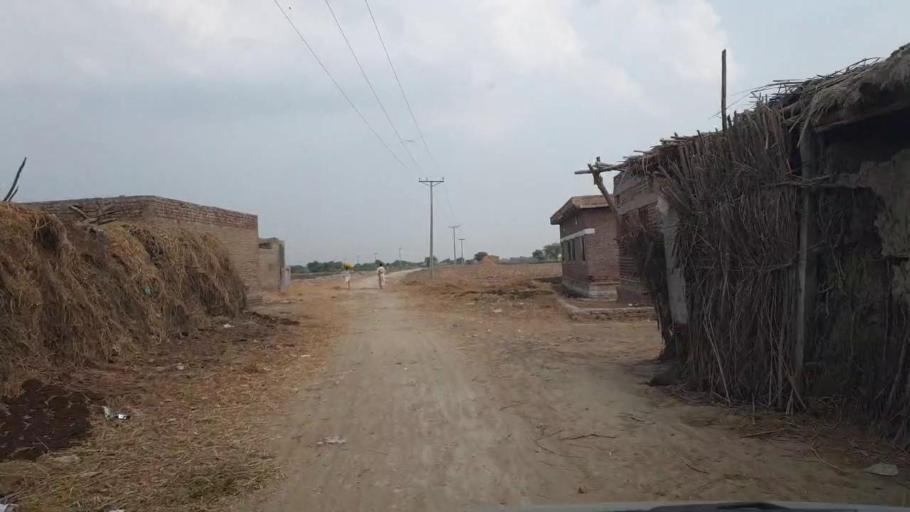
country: PK
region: Sindh
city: Matli
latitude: 24.9561
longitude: 68.7136
